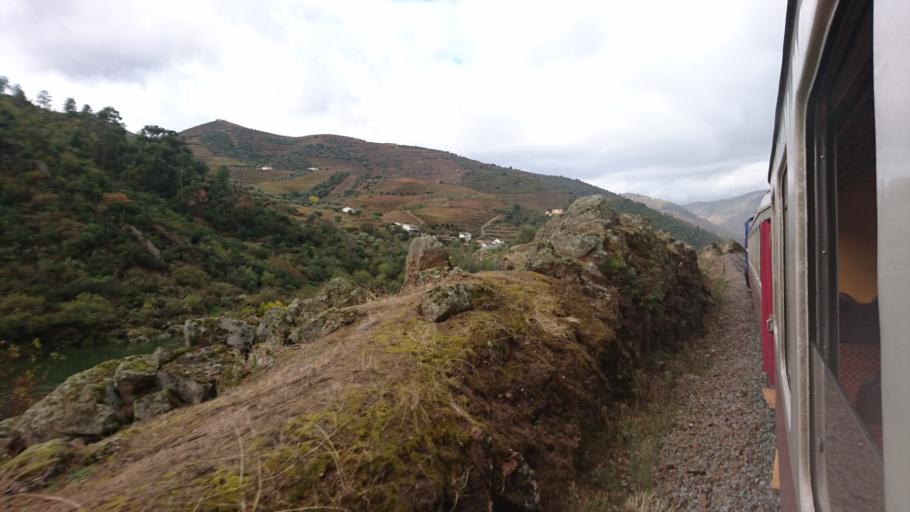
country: PT
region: Viseu
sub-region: Sao Joao da Pesqueira
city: Sao Joao da Pesqueira
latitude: 41.1996
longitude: -7.4001
